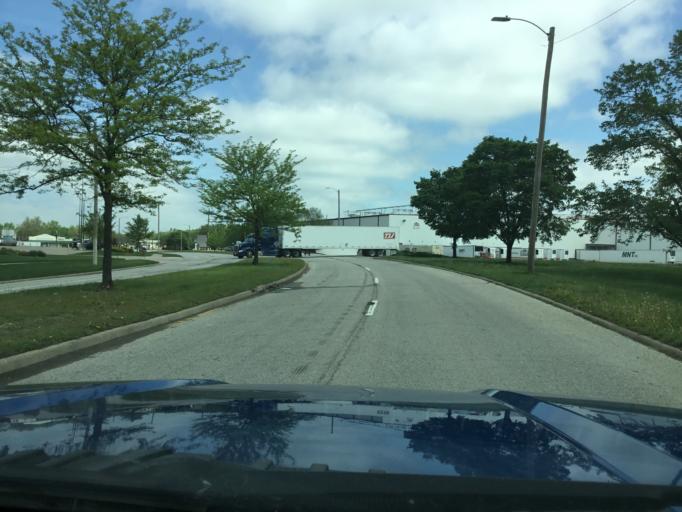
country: US
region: Kansas
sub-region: Shawnee County
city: Topeka
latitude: 39.0416
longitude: -95.6354
